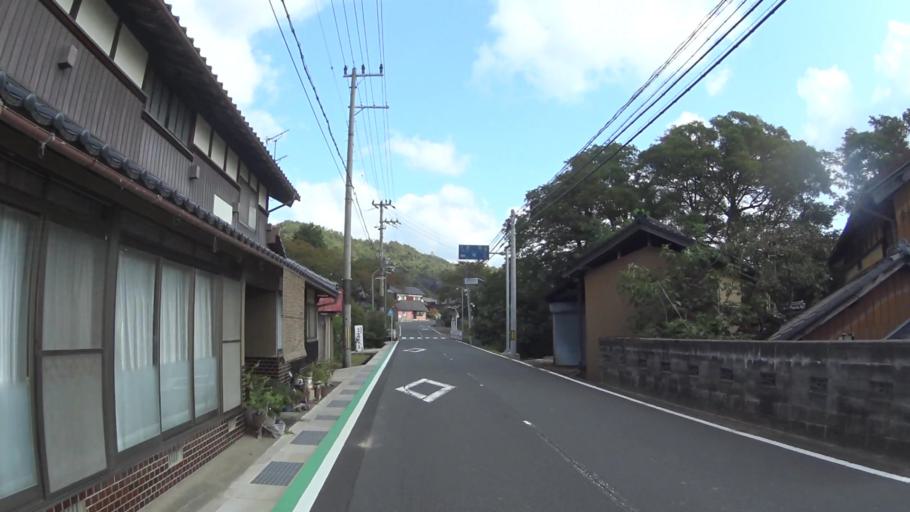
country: JP
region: Kyoto
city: Miyazu
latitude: 35.6090
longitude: 135.2213
